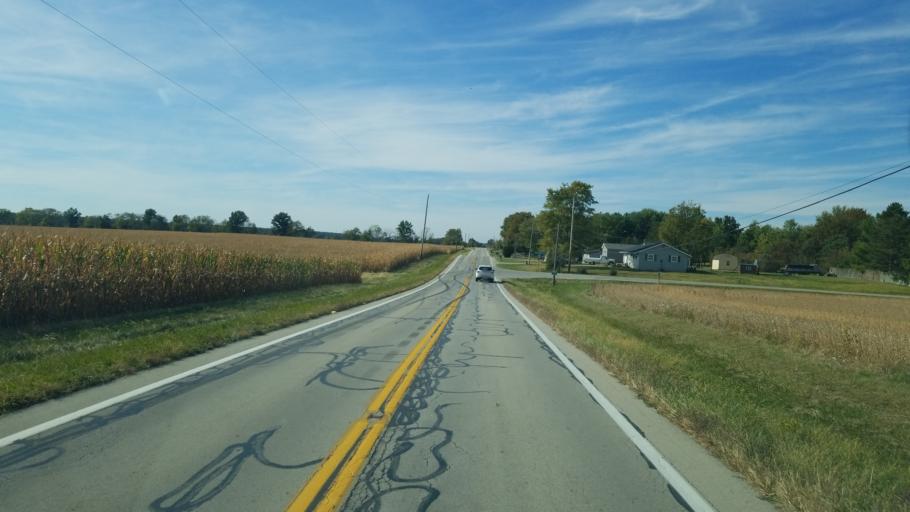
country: US
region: Ohio
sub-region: Clinton County
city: Wilmington
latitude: 39.3697
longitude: -83.8899
